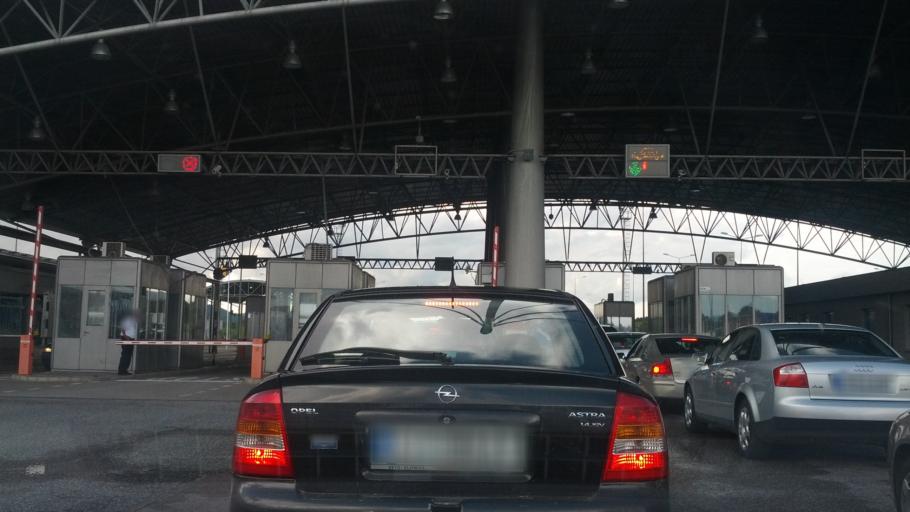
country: BA
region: Federation of Bosnia and Herzegovina
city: Izacic
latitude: 44.8751
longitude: 15.7643
